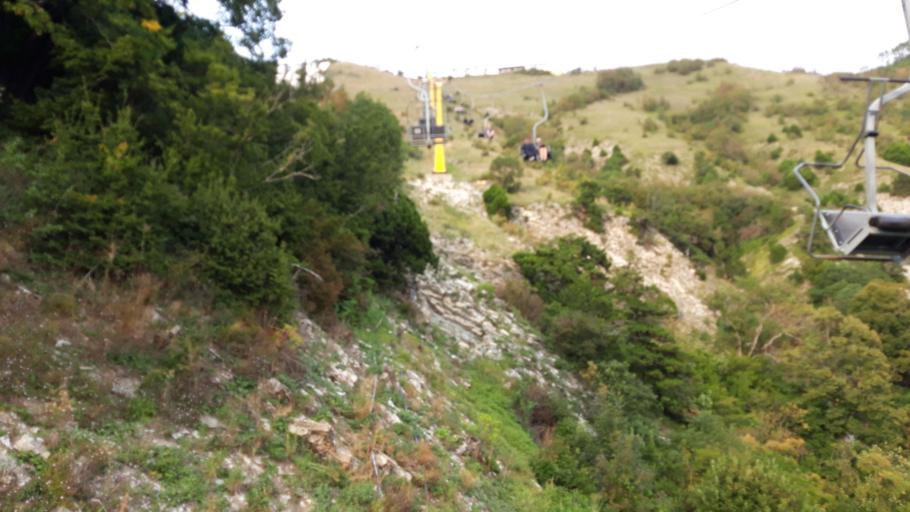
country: RU
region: Krasnodarskiy
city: Gelendzhik
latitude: 44.5823
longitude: 38.0983
